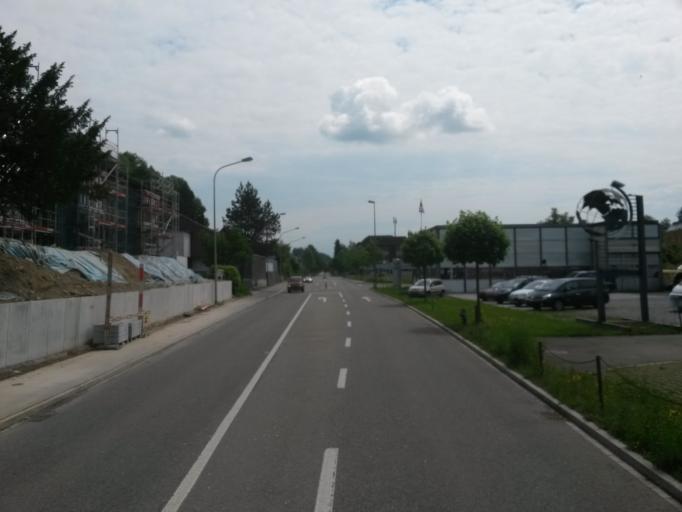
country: CH
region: Zurich
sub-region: Bezirk Pfaeffikon
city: Illnau
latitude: 47.4131
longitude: 8.7223
